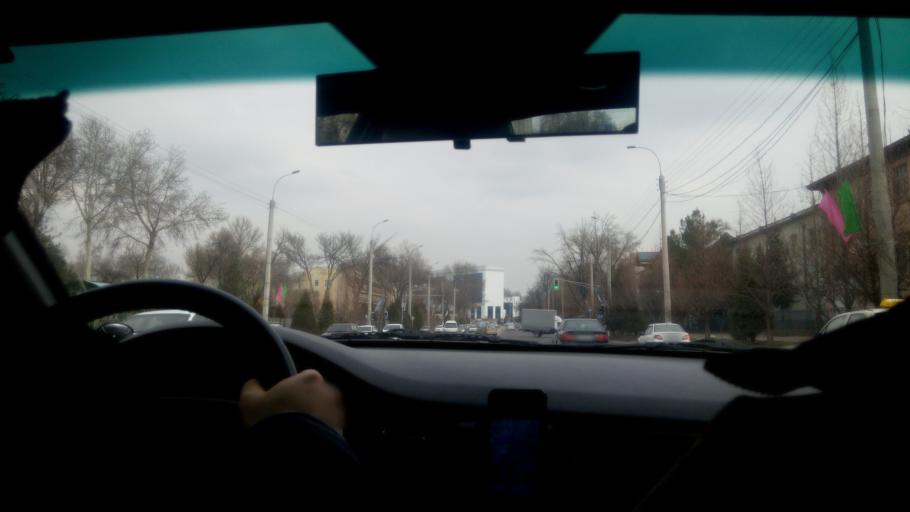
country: UZ
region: Toshkent
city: Salor
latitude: 41.3373
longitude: 69.3283
